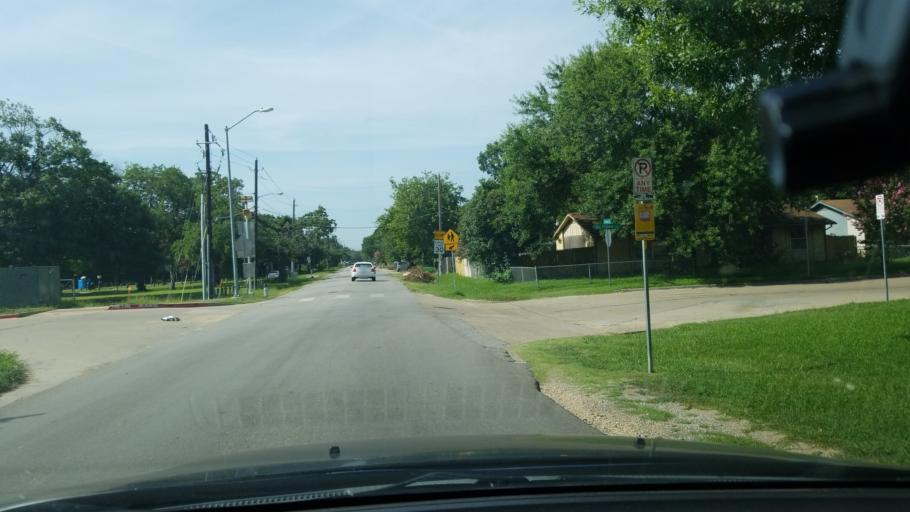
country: US
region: Texas
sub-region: Dallas County
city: Balch Springs
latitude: 32.7252
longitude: -96.6393
